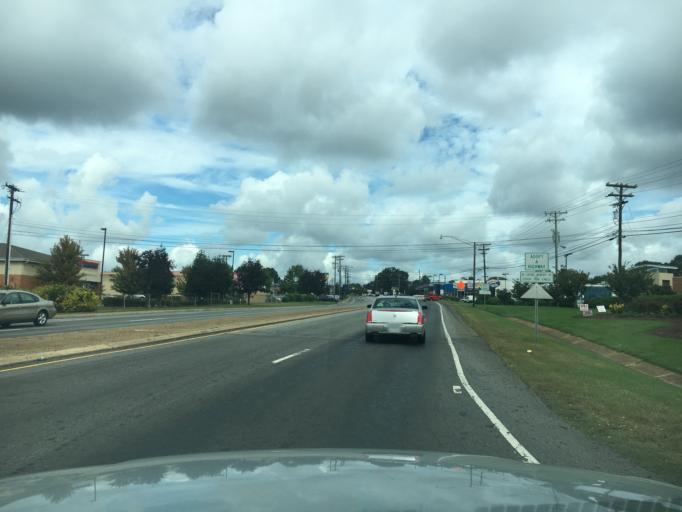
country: US
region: North Carolina
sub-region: Catawba County
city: Hickory
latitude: 35.7149
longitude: -81.3131
